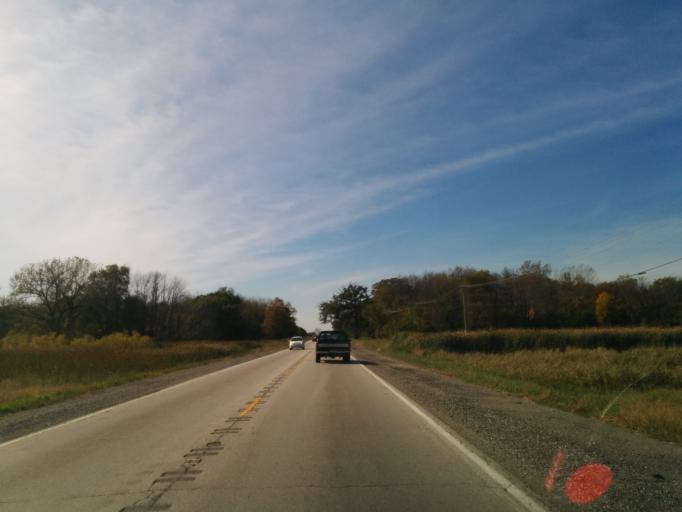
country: US
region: Illinois
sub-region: DuPage County
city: Warrenville
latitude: 41.8189
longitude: -88.2386
